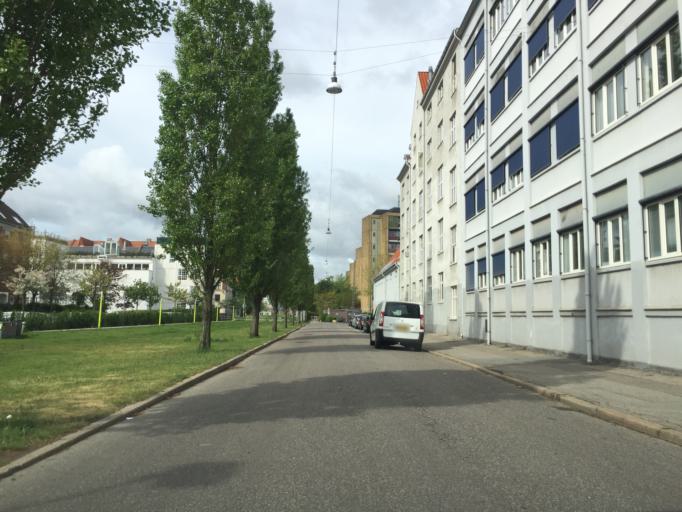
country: DK
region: Capital Region
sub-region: Kobenhavn
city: Christianshavn
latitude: 55.6665
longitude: 12.6078
